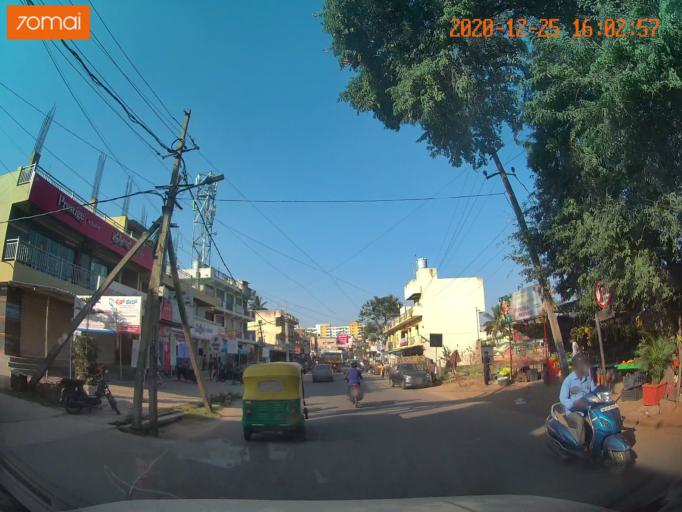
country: IN
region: Karnataka
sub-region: Bangalore Urban
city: Bangalore
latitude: 12.8832
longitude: 77.6248
